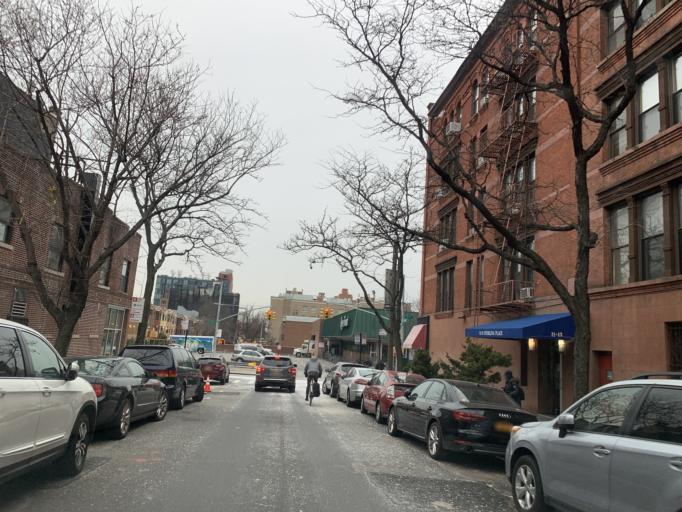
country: US
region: New York
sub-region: Kings County
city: Brooklyn
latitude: 40.6789
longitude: -73.9781
